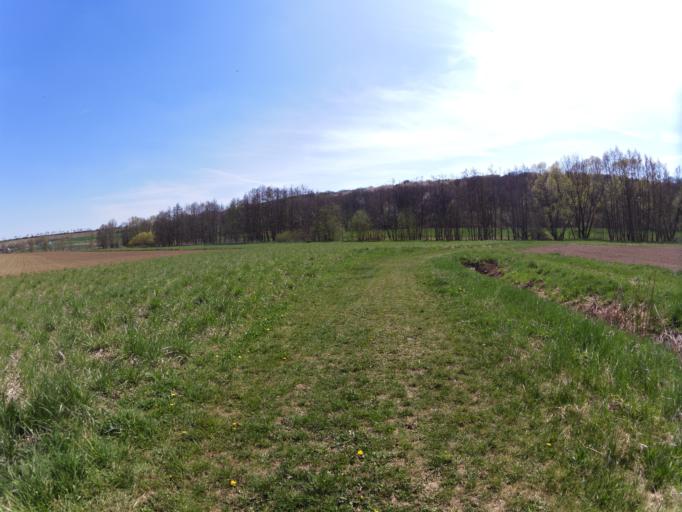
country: DE
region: Bavaria
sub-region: Regierungsbezirk Unterfranken
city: Estenfeld
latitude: 49.8574
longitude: 10.0024
